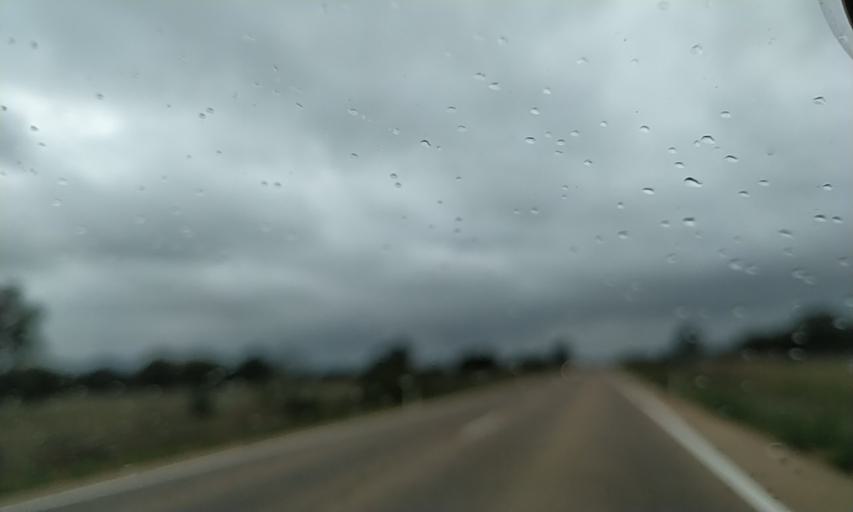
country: ES
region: Extremadura
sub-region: Provincia de Badajoz
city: Villar del Rey
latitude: 38.9908
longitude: -6.8748
